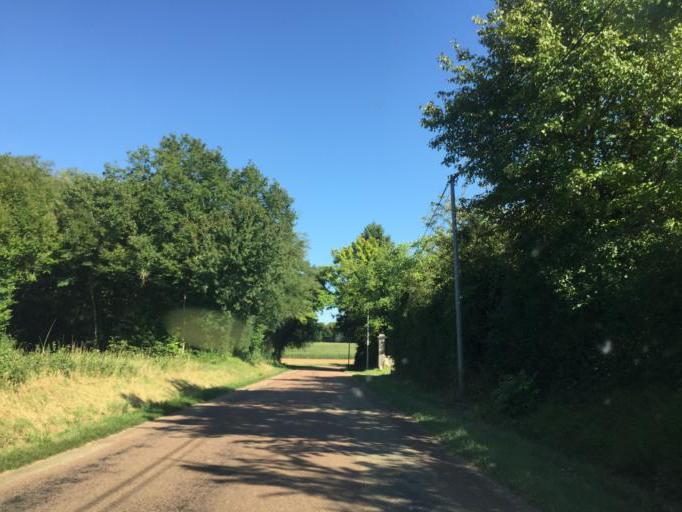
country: FR
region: Bourgogne
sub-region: Departement de l'Yonne
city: Fontenailles
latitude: 47.4979
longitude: 3.3669
